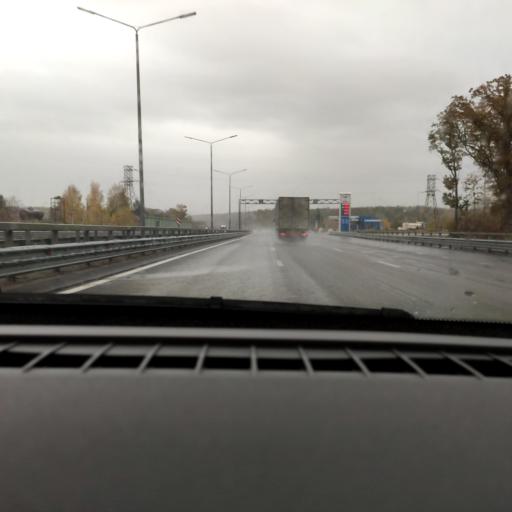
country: RU
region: Voronezj
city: Podgornoye
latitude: 51.8146
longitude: 39.2521
